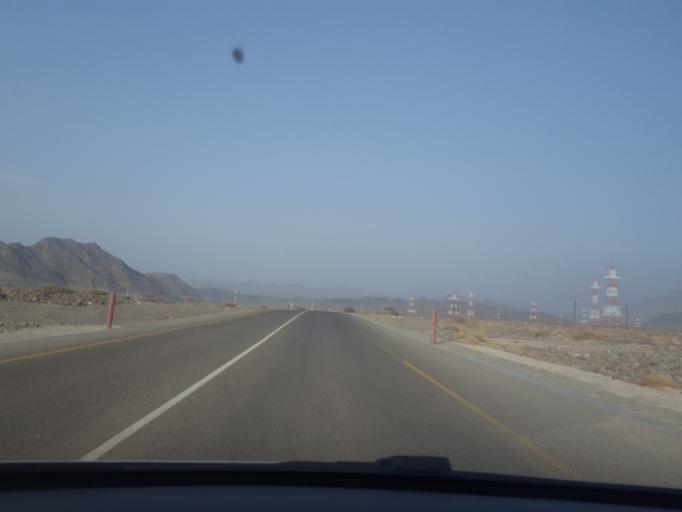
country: AE
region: Abu Dhabi
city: Al Ain
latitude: 24.0480
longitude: 56.0486
